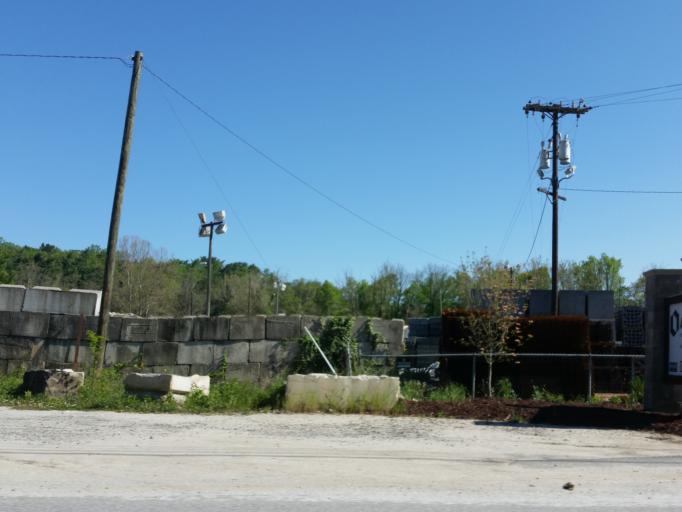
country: US
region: North Carolina
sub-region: Buncombe County
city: Asheville
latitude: 35.5661
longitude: -82.5547
